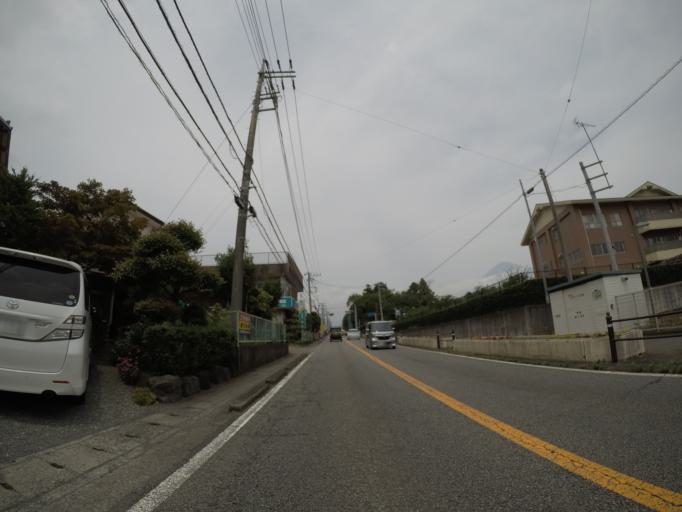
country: JP
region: Shizuoka
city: Fujinomiya
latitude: 35.2366
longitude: 138.6094
